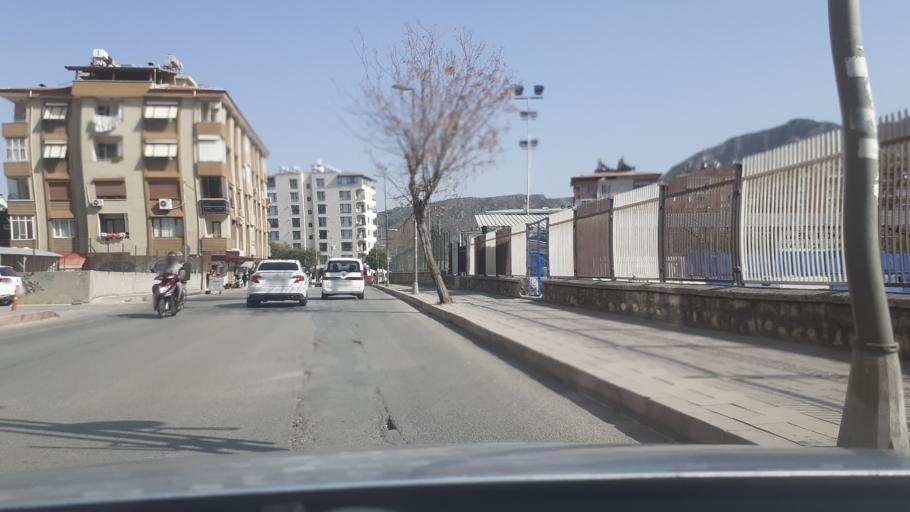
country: TR
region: Hatay
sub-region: Antakya Ilcesi
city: Antakya
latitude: 36.2127
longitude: 36.1584
